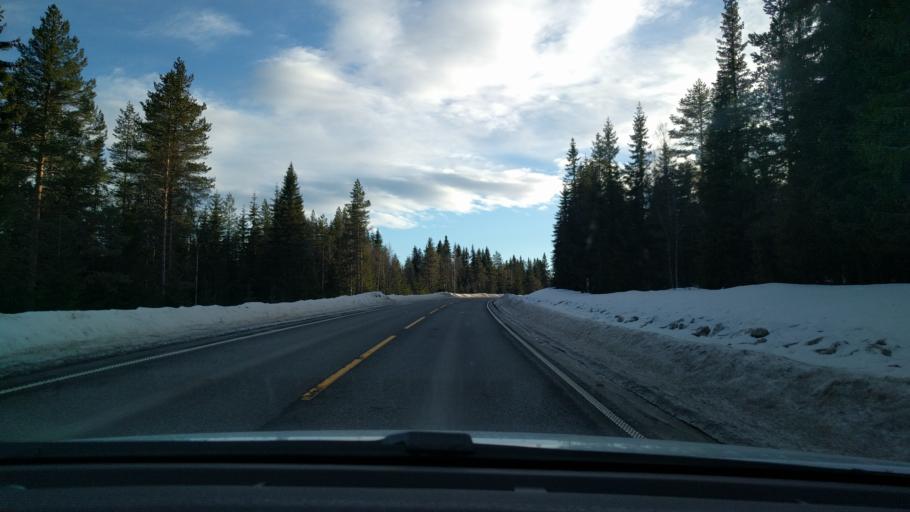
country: NO
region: Hedmark
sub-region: Trysil
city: Innbygda
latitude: 61.0644
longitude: 11.9689
